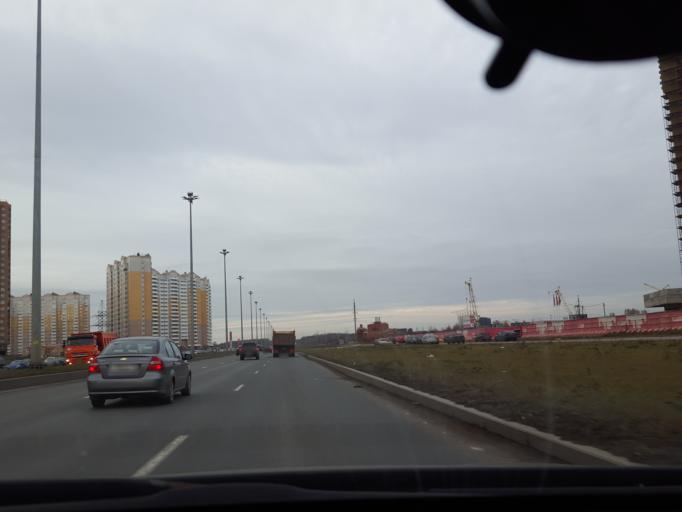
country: RU
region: St.-Petersburg
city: Kolomyagi
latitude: 60.0334
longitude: 30.2499
